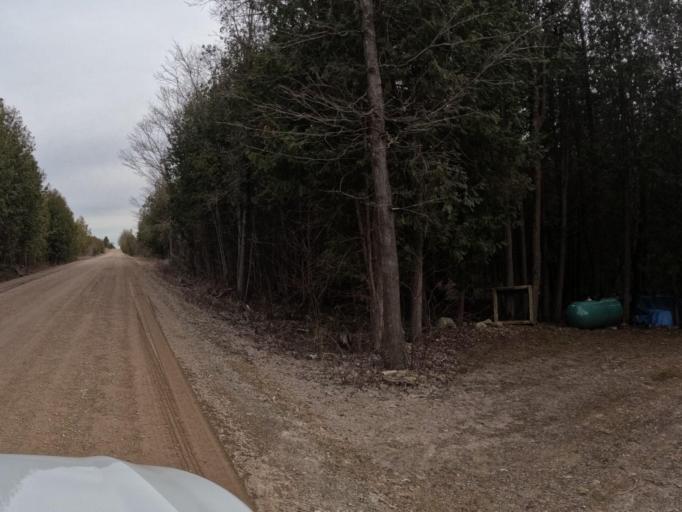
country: CA
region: Ontario
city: Shelburne
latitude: 43.9386
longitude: -80.2596
